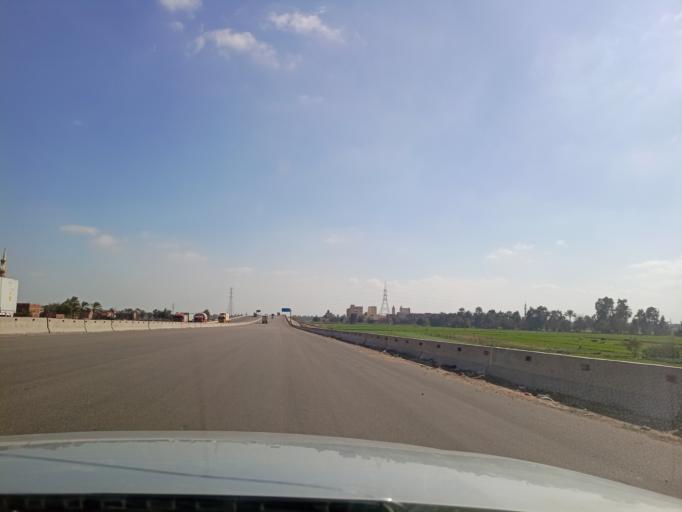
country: EG
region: Eastern Province
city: Mashtul as Suq
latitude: 30.4618
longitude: 31.3262
